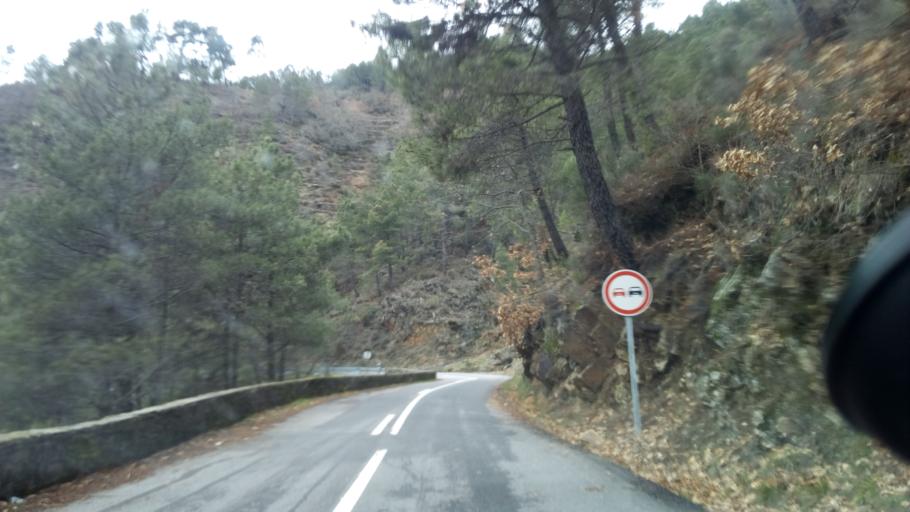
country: PT
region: Guarda
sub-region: Manteigas
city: Manteigas
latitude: 40.4163
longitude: -7.5276
